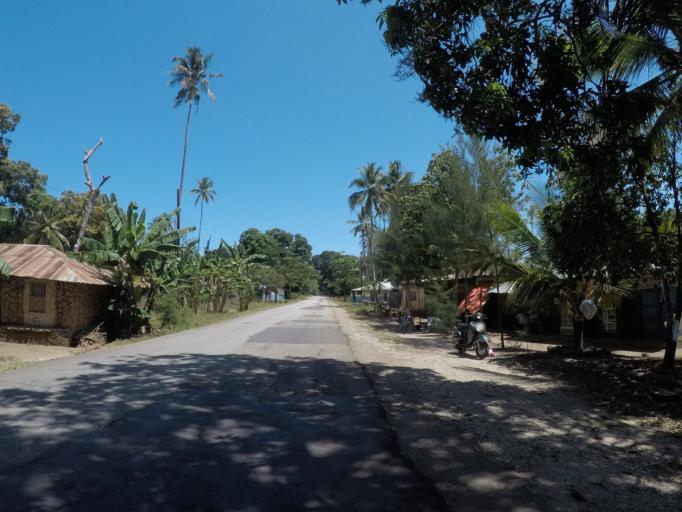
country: TZ
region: Zanzibar Central/South
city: Nganane
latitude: -6.2940
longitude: 39.4377
